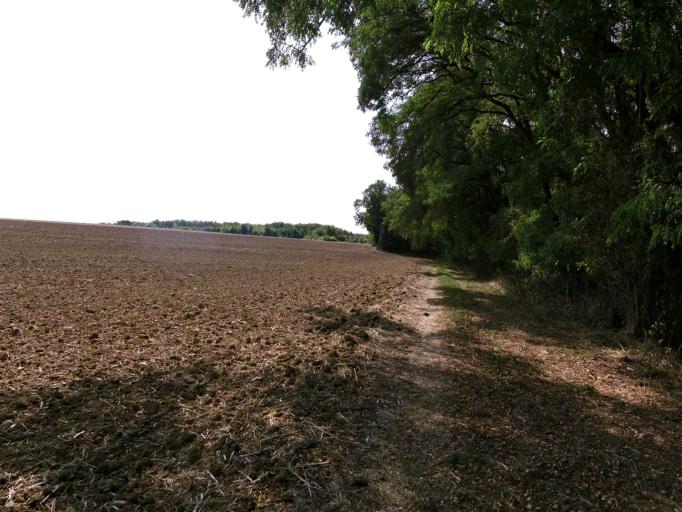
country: DE
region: Bavaria
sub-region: Regierungsbezirk Unterfranken
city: Gerbrunn
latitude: 49.7607
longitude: 10.0092
